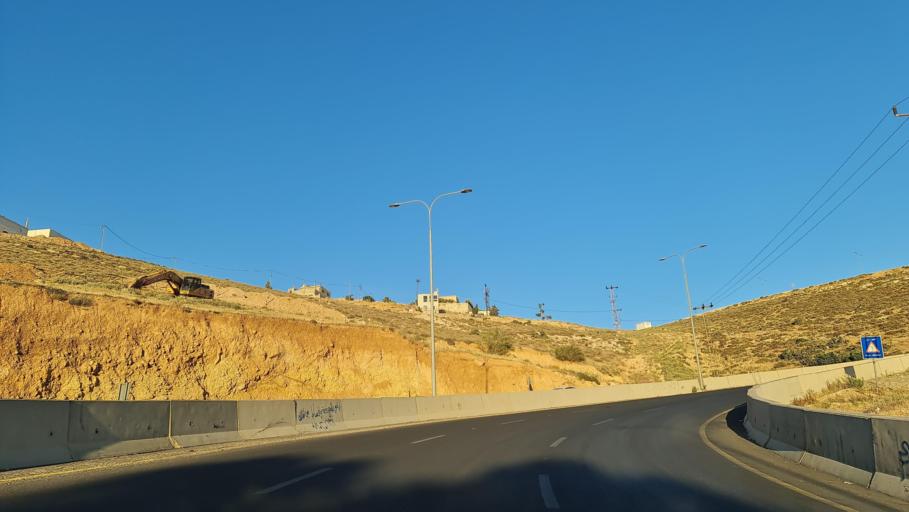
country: JO
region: Zarqa
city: Russeifa
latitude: 32.0939
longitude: 35.9614
